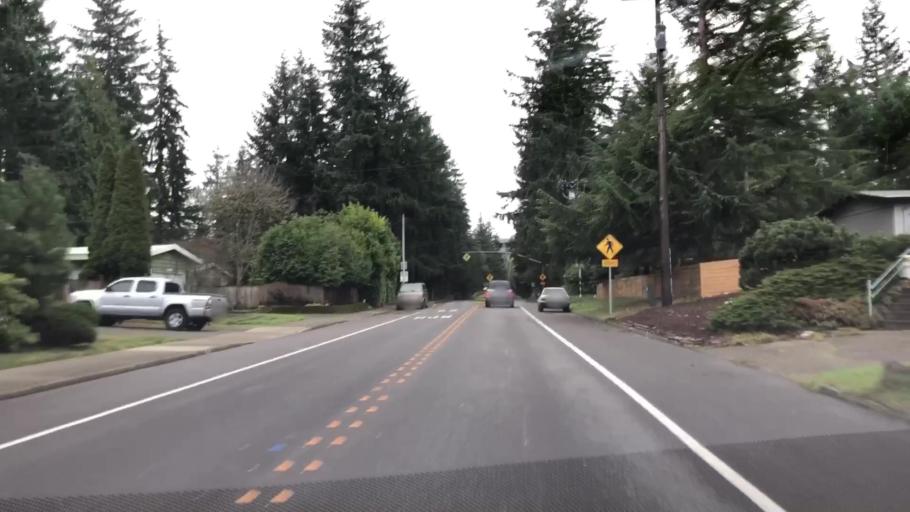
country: US
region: Washington
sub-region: King County
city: Eastgate
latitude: 47.5866
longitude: -122.1325
